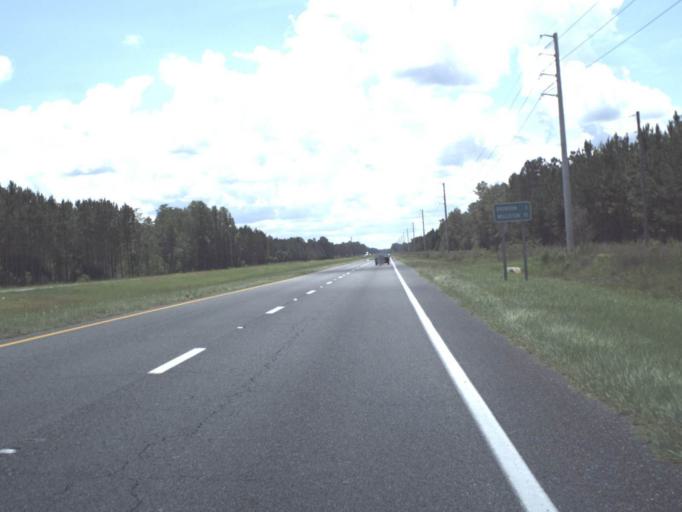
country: US
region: Florida
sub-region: Levy County
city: Bronson
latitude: 29.4749
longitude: -82.6810
